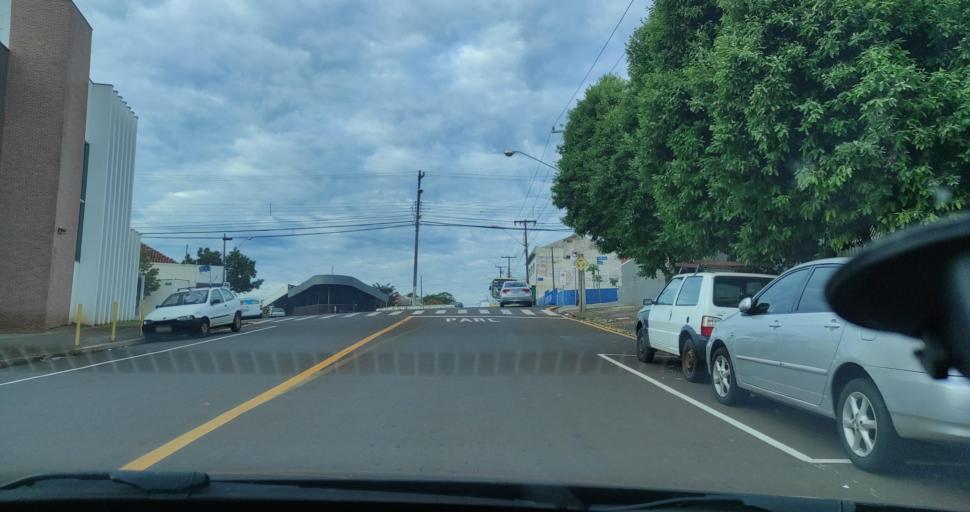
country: BR
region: Parana
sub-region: Ibipora
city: Ibipora
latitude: -23.2671
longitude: -51.0444
